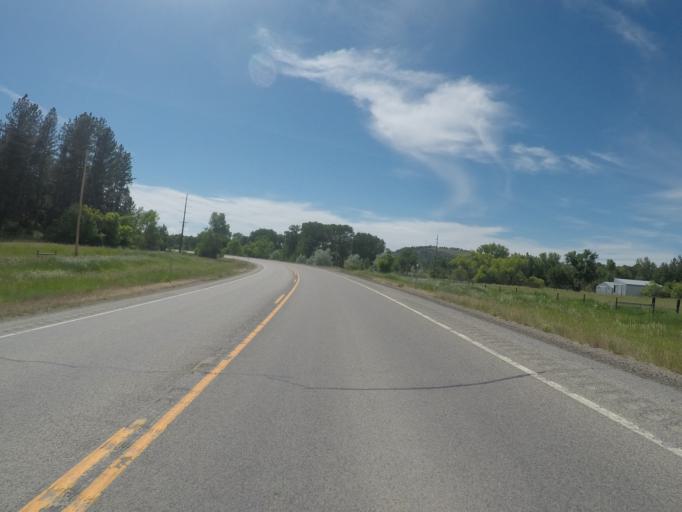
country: US
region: Montana
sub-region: Stillwater County
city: Columbus
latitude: 45.6325
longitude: -109.2726
